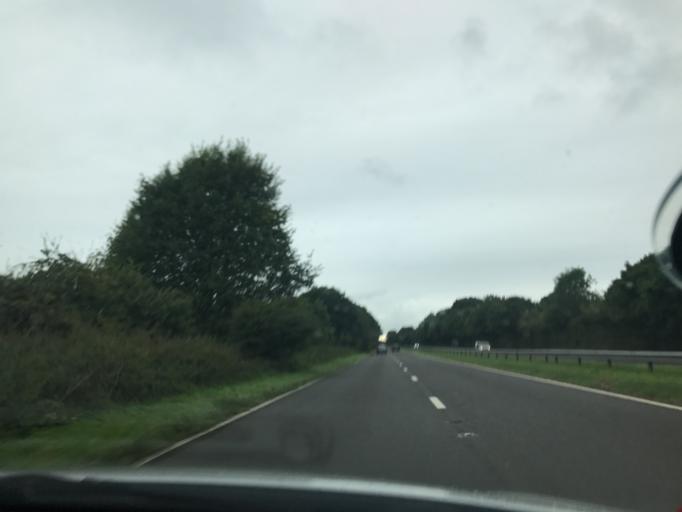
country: GB
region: England
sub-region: Cheshire West and Chester
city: Hartford
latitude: 53.2382
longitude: -2.5571
